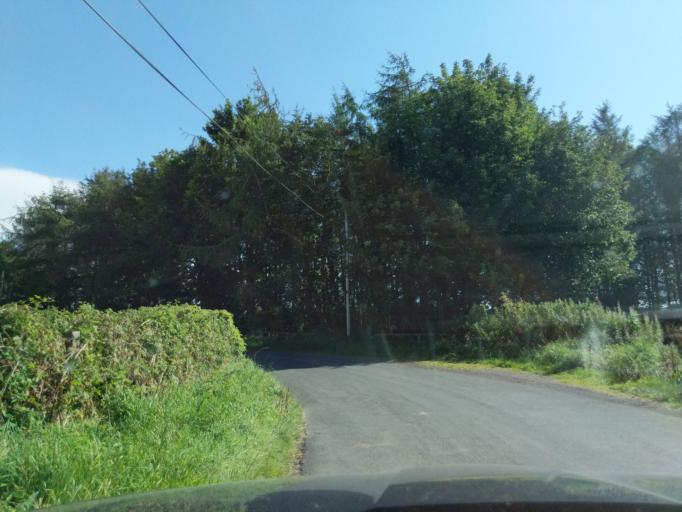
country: GB
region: Scotland
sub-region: The Scottish Borders
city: Coldstream
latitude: 55.6732
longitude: -2.1863
